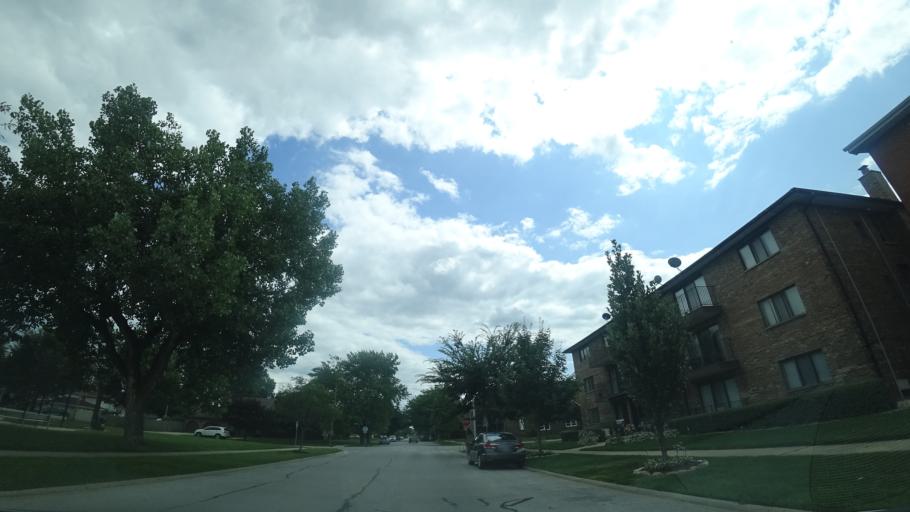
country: US
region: Illinois
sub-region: Cook County
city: Oak Lawn
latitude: 41.6951
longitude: -87.7374
